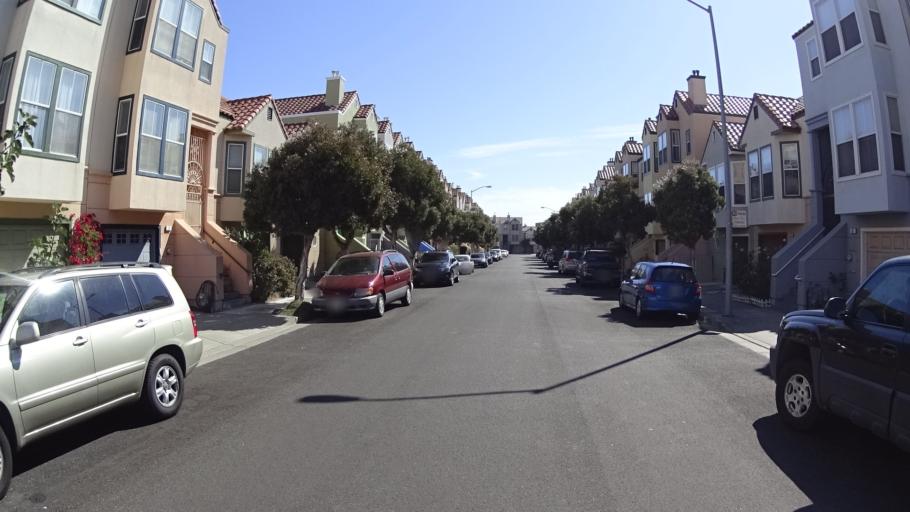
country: US
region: California
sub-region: San Mateo County
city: Brisbane
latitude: 37.7277
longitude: -122.3986
